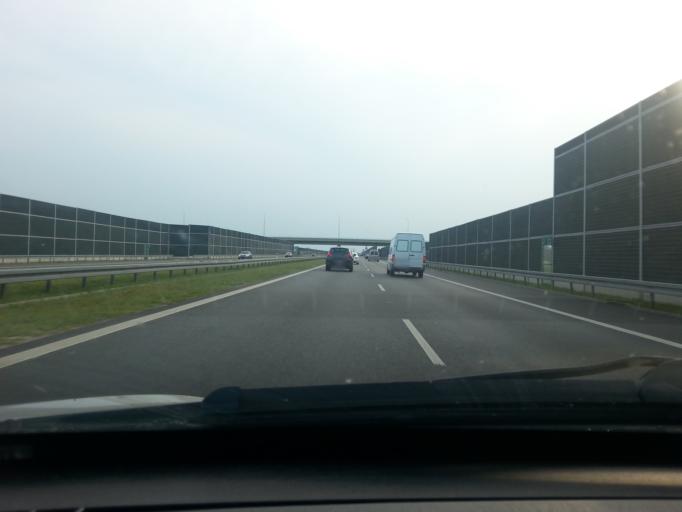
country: PL
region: Masovian Voivodeship
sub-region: Powiat zyrardowski
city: Zyrardow
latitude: 52.1155
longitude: 20.4891
